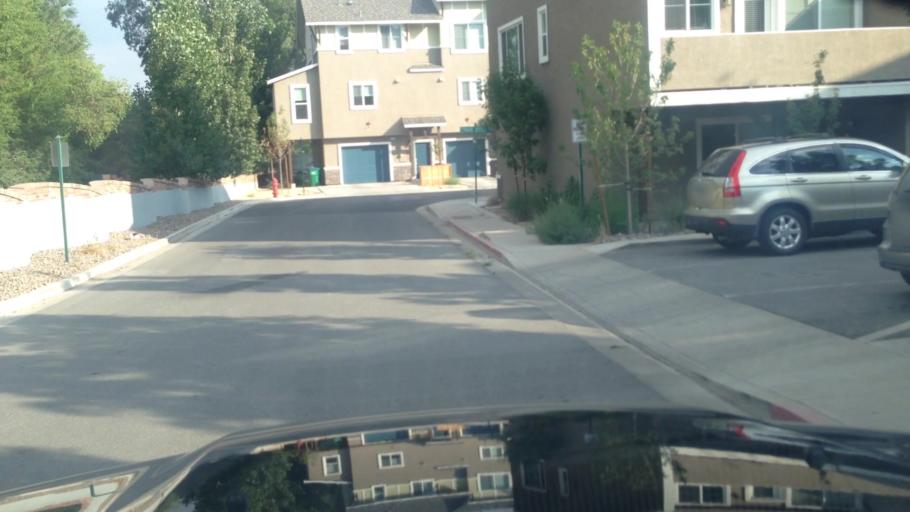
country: US
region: Nevada
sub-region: Washoe County
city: Reno
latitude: 39.5195
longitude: -119.8430
